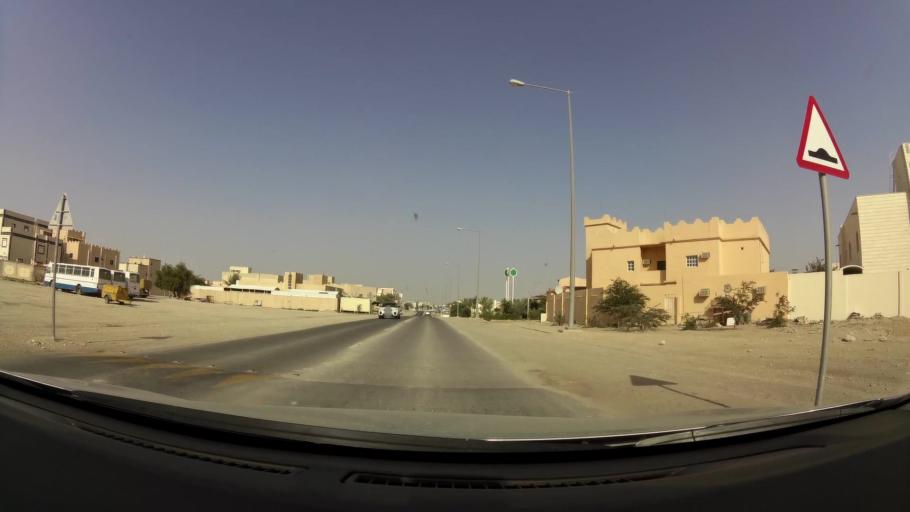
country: QA
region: Baladiyat ar Rayyan
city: Ar Rayyan
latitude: 25.3395
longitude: 51.4278
